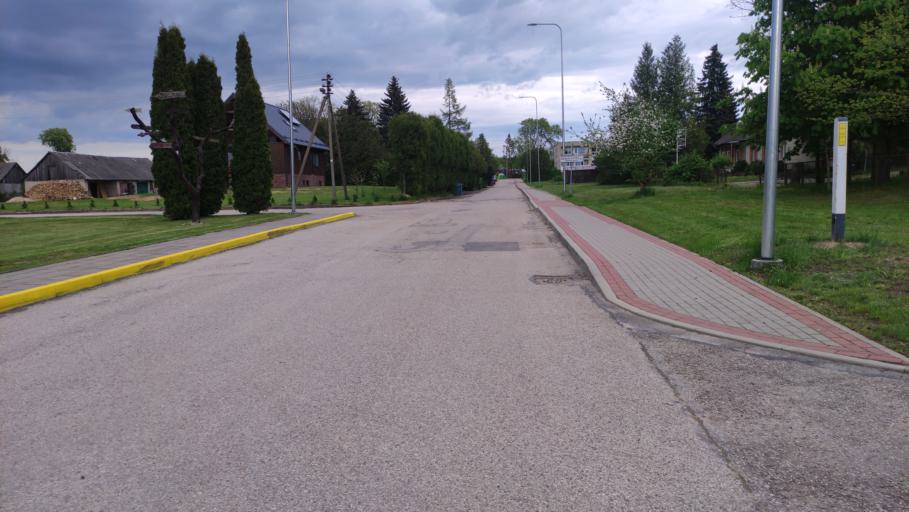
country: LT
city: Jieznas
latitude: 54.5034
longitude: 24.2513
